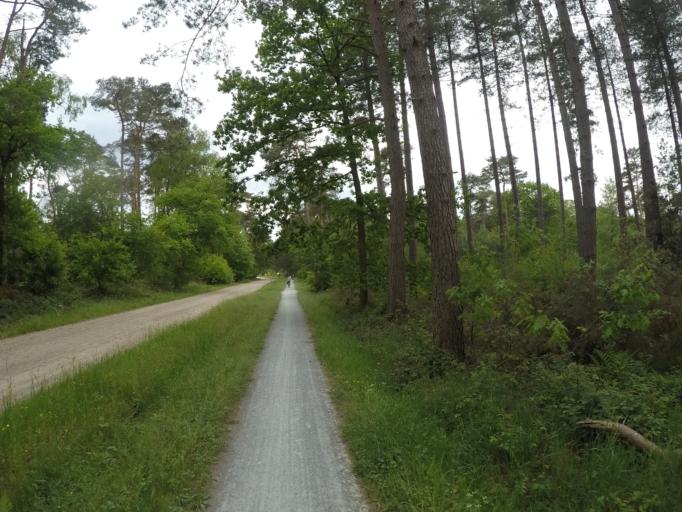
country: BE
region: Flanders
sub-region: Provincie Antwerpen
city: Oostmalle
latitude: 51.2810
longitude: 4.7416
